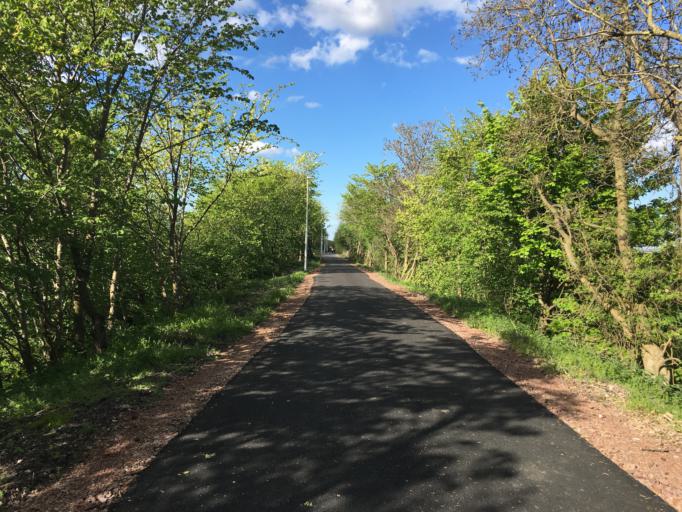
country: GB
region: Scotland
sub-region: Midlothian
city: Loanhead
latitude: 55.8946
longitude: -3.1330
